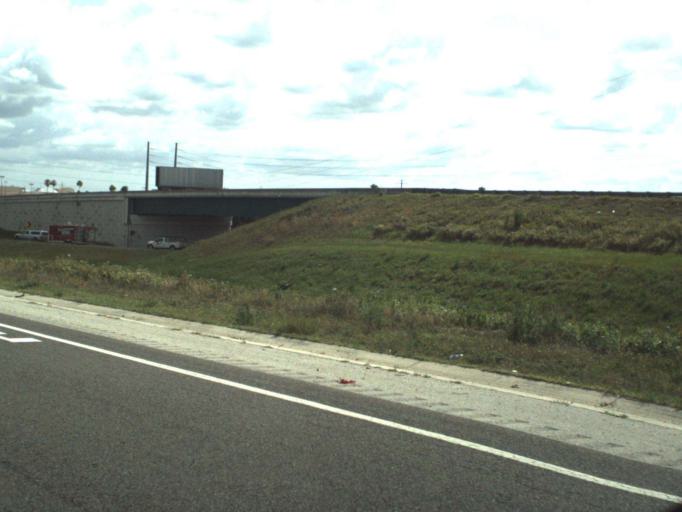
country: US
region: Florida
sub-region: Seminole County
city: Heathrow
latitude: 28.7982
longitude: -81.3444
